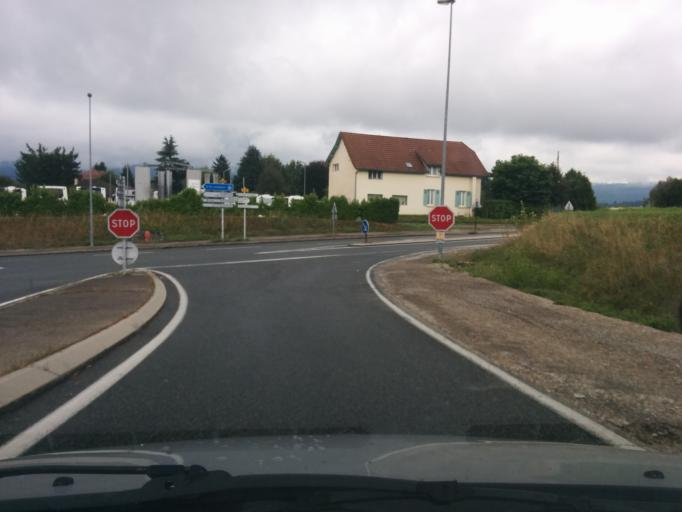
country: FR
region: Rhone-Alpes
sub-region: Departement de la Savoie
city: Le Pont-de-Beauvoisin
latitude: 45.5276
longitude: 5.6797
